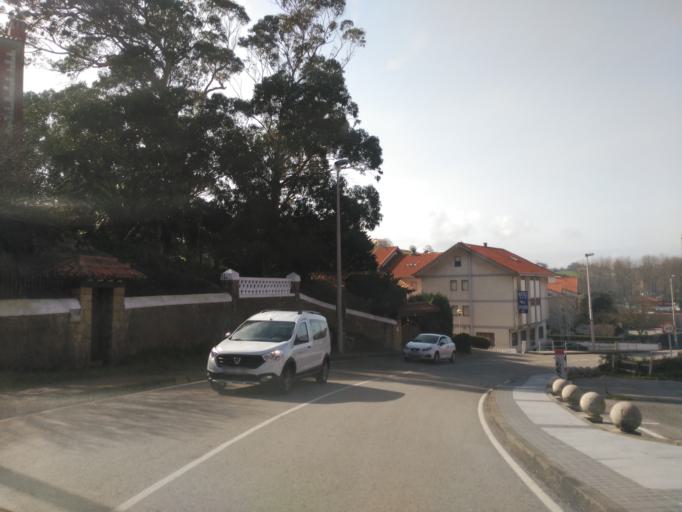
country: ES
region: Cantabria
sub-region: Provincia de Cantabria
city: Suances
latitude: 43.4331
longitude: -4.0413
